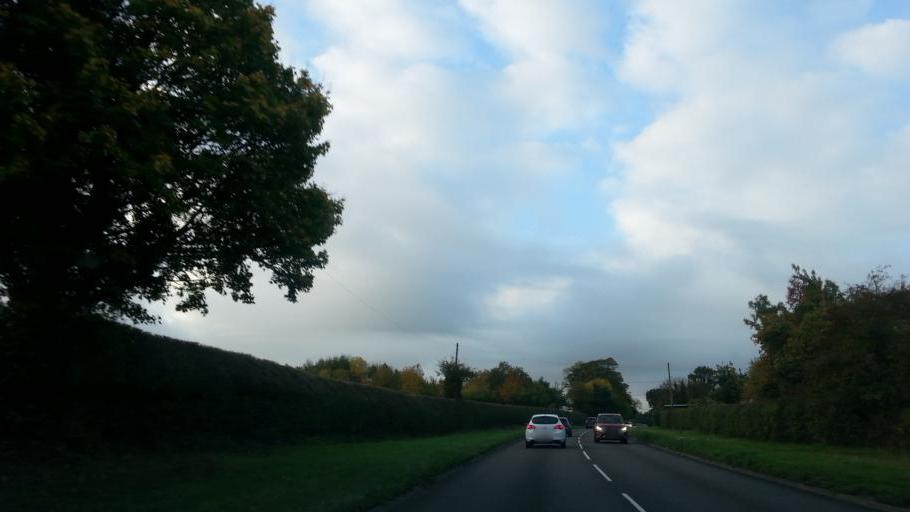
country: GB
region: England
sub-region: Staffordshire
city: Fazeley
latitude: 52.6085
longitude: -1.7477
